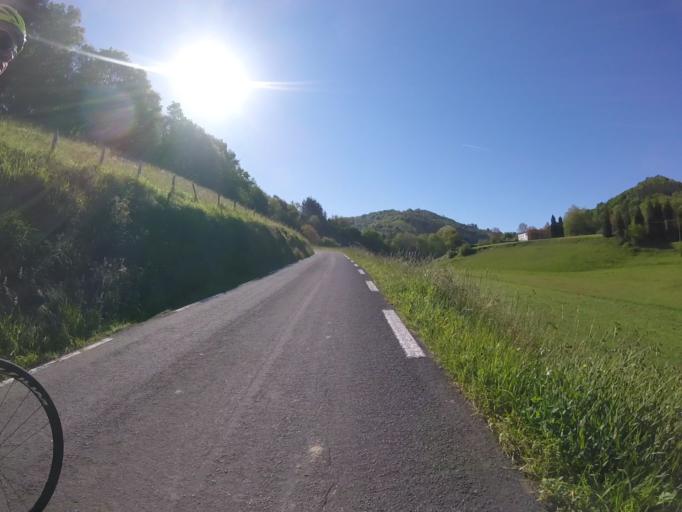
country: ES
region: Basque Country
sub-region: Provincia de Guipuzcoa
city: Aizarnazabal
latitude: 43.2301
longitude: -2.2172
